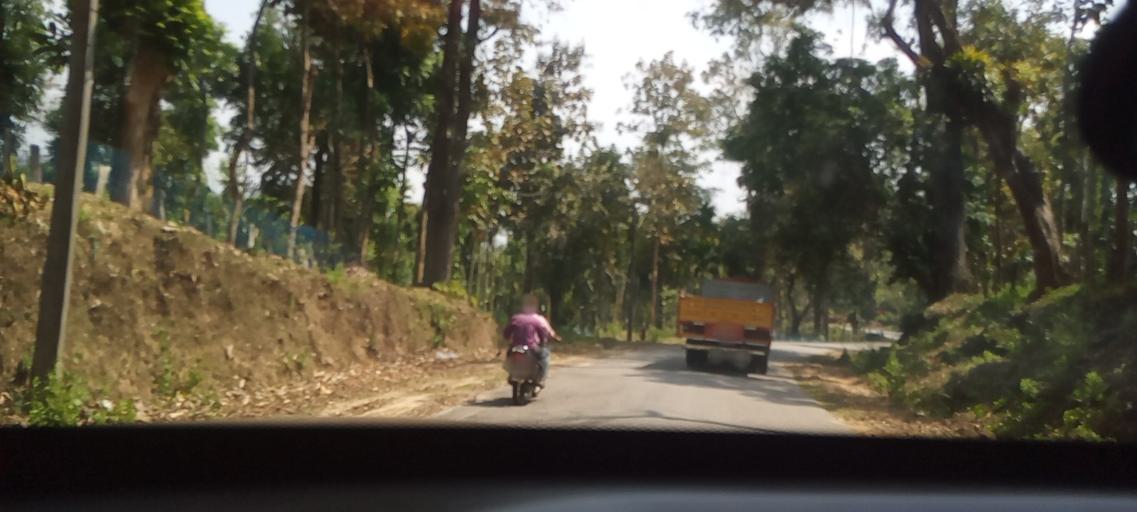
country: IN
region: Karnataka
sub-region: Chikmagalur
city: Mudigere
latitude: 13.3155
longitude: 75.5706
